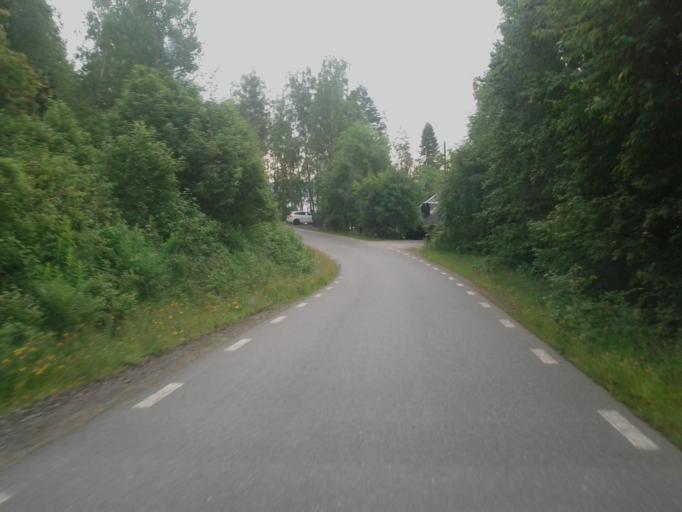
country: SE
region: Vaesternorrland
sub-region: Kramfors Kommun
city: Nordingra
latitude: 63.0617
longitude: 18.3938
